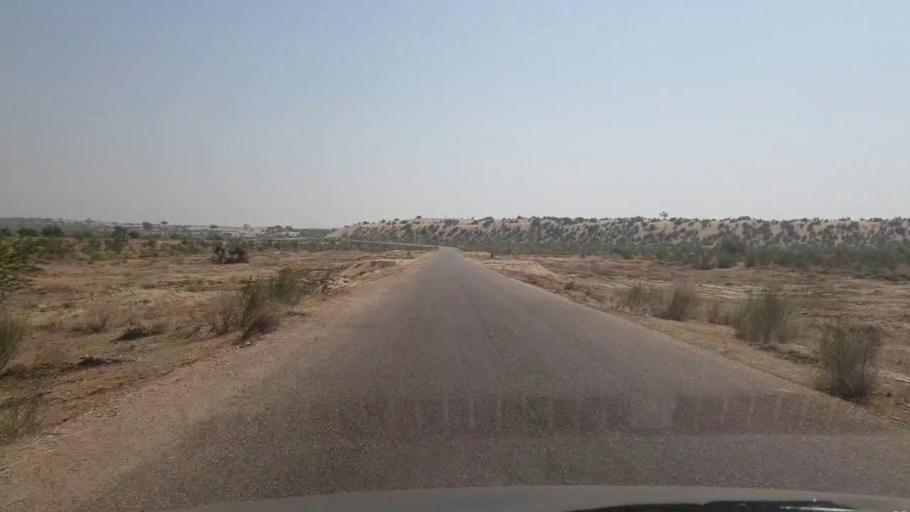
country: PK
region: Sindh
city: Chor
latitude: 25.6712
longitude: 70.1511
